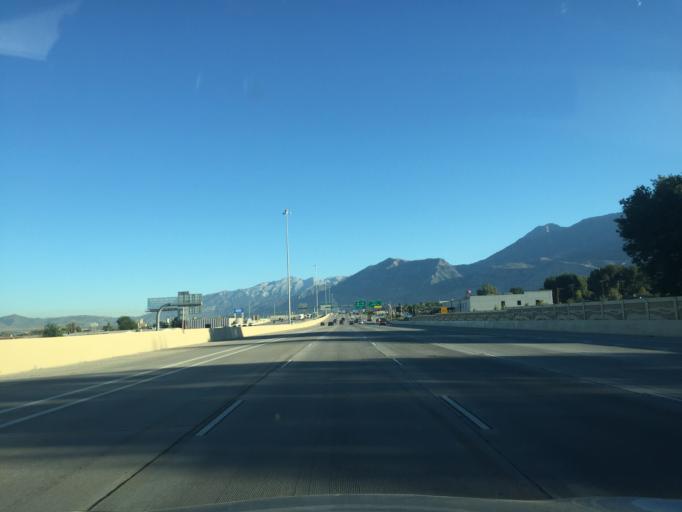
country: US
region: Utah
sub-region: Utah County
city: Orem
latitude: 40.2906
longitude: -111.7255
